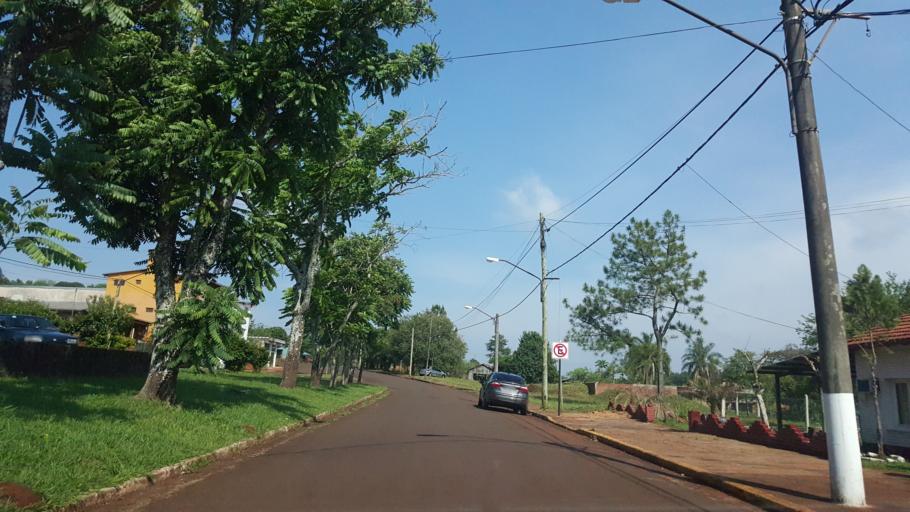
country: AR
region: Misiones
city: Capiovi
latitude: -26.9289
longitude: -55.0626
